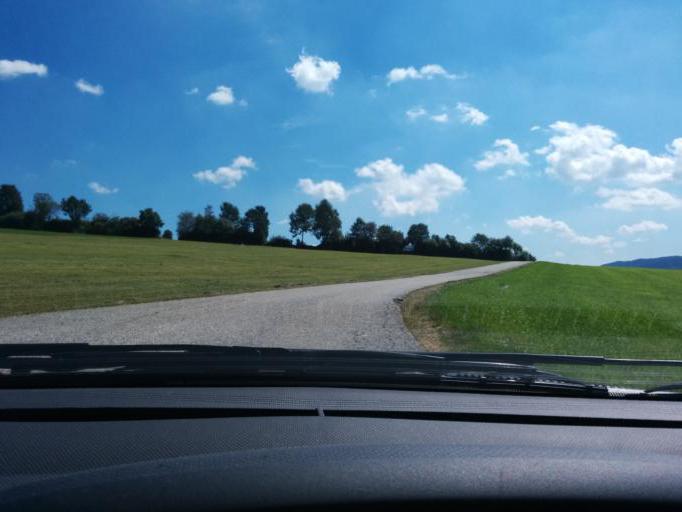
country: AT
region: Upper Austria
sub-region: Politischer Bezirk Rohrbach
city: Ulrichsberg
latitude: 48.6941
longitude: 13.9071
